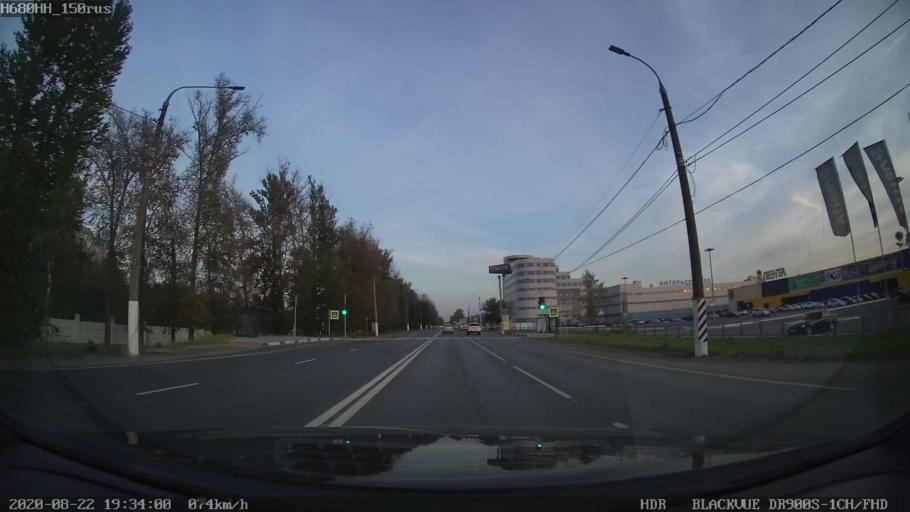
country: RU
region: Tverskaya
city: Tver
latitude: 56.8449
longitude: 35.9492
